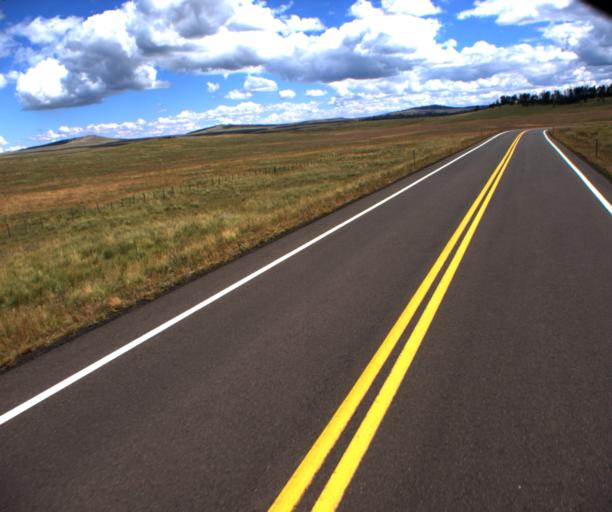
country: US
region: Arizona
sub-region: Apache County
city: Eagar
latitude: 33.9207
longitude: -109.4346
